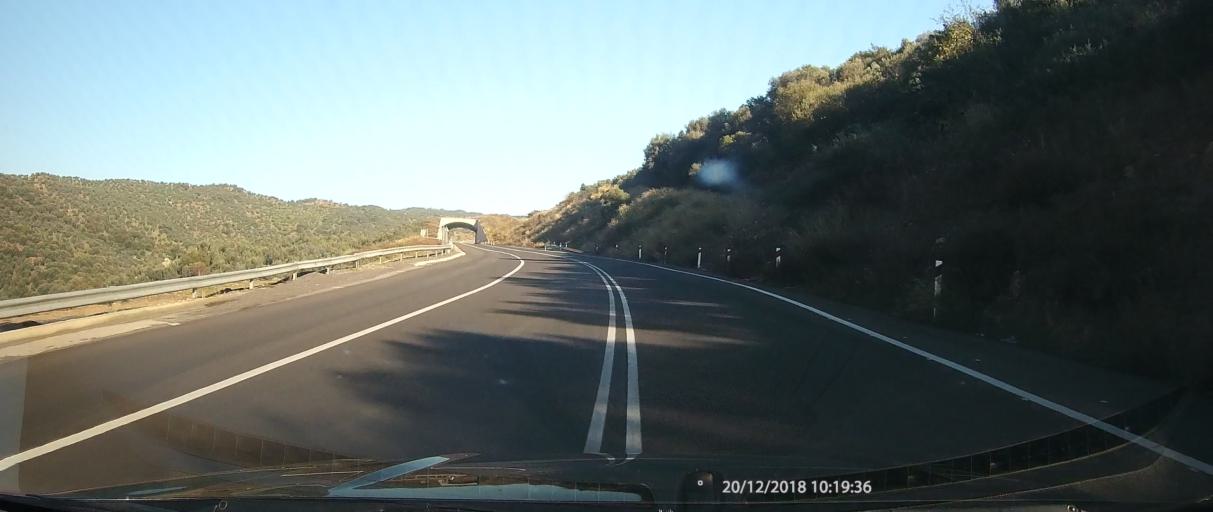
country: GR
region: Peloponnese
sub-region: Nomos Lakonias
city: Magoula
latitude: 37.1365
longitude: 22.4246
